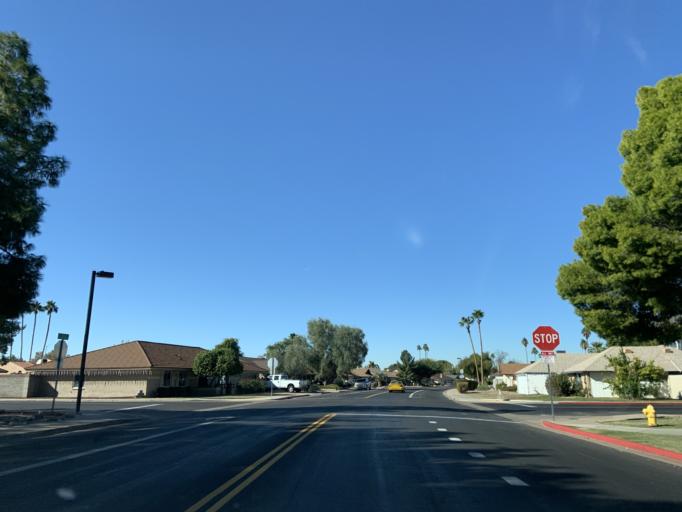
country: US
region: Arizona
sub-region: Maricopa County
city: San Carlos
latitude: 33.3659
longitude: -111.8712
